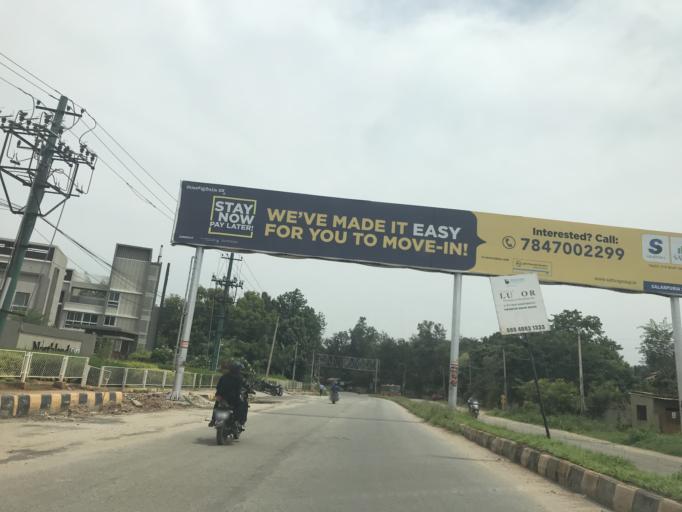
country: IN
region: Karnataka
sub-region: Bangalore Urban
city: Yelahanka
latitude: 13.0829
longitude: 77.6538
